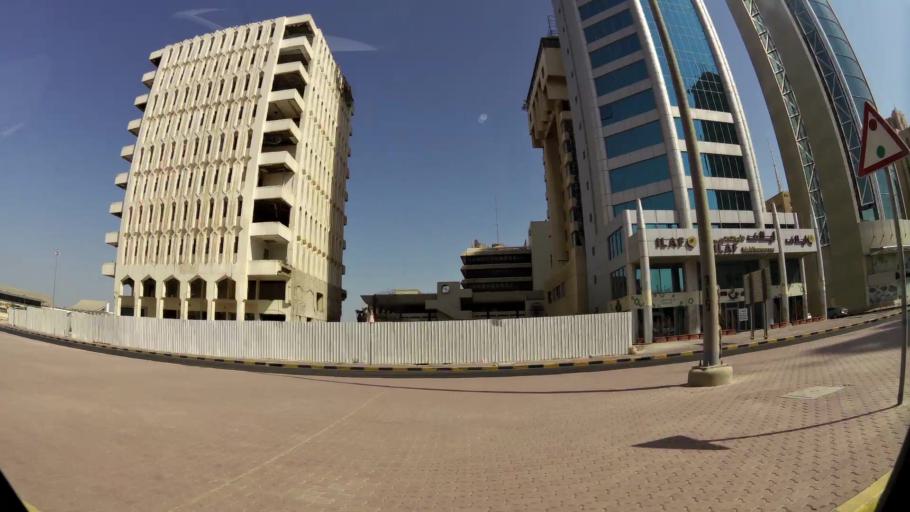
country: KW
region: Al Asimah
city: Kuwait City
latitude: 29.3664
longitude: 47.9654
